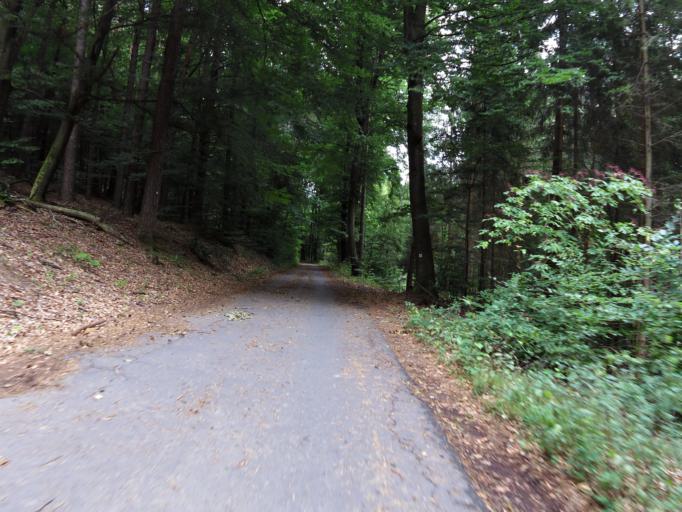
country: DE
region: Hesse
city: Hochst im Odenwald
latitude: 49.7809
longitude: 8.9717
